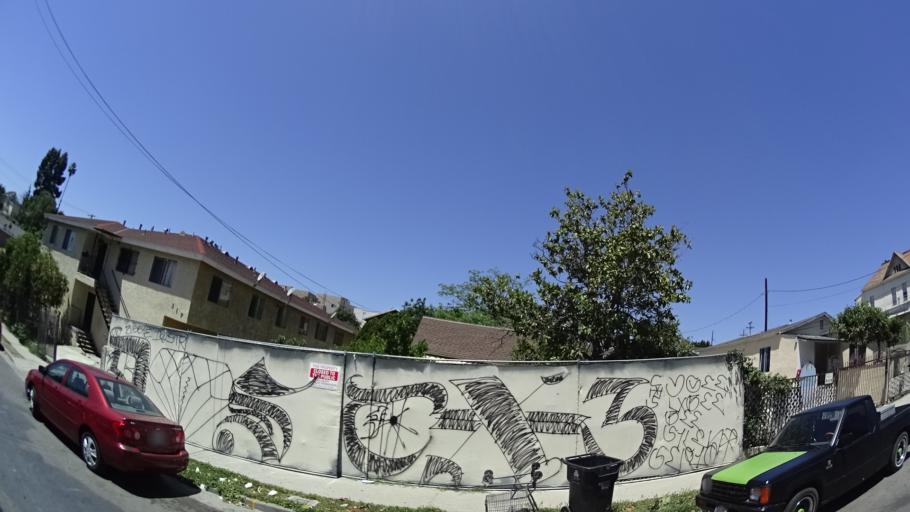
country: US
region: California
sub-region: Los Angeles County
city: Echo Park
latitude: 34.0641
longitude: -118.2551
